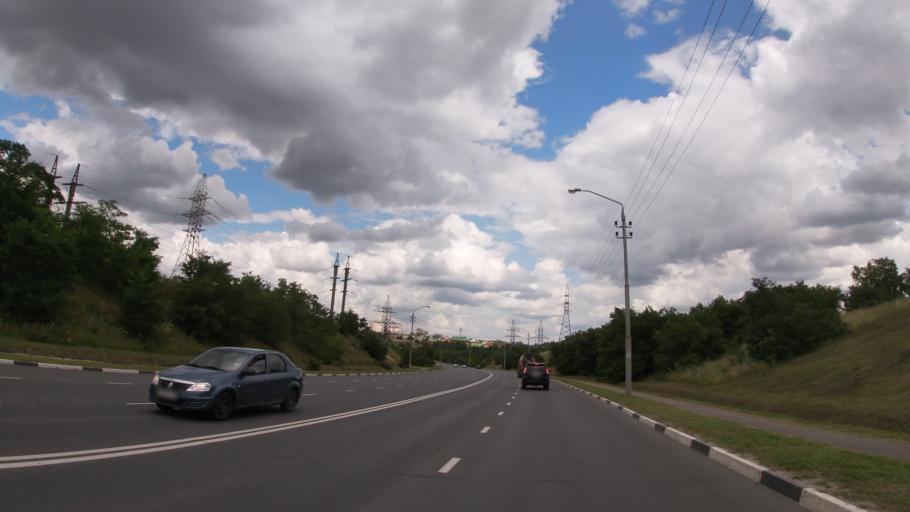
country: RU
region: Belgorod
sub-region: Belgorodskiy Rayon
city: Belgorod
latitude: 50.5563
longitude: 36.5849
